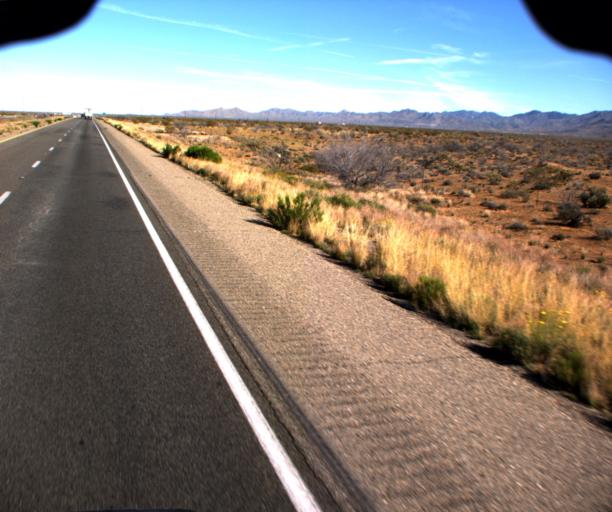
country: US
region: Arizona
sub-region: Mohave County
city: Golden Valley
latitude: 35.3138
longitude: -114.1990
